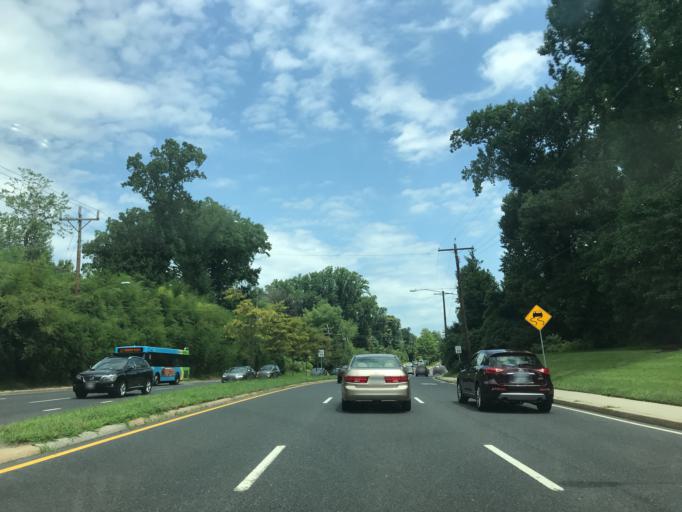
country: US
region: Maryland
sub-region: Montgomery County
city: South Kensington
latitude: 39.0114
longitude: -77.0808
